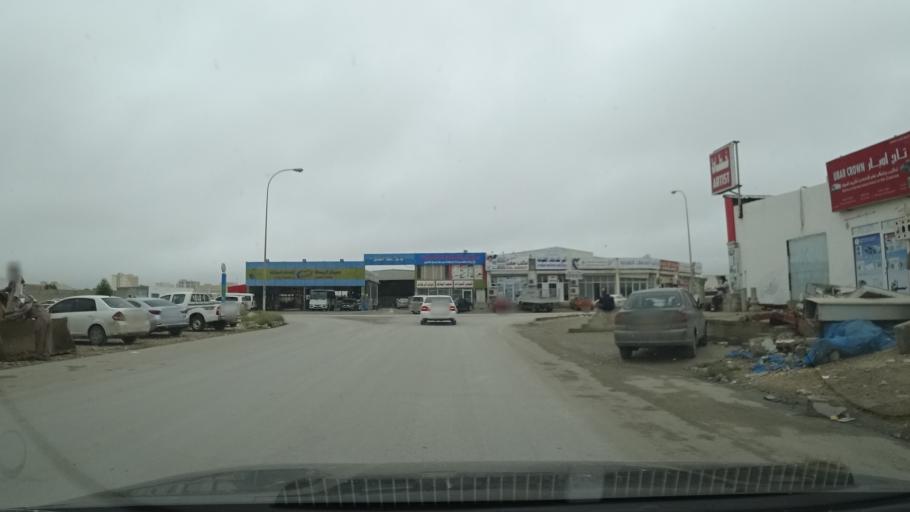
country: OM
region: Zufar
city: Salalah
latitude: 17.0183
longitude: 54.0415
